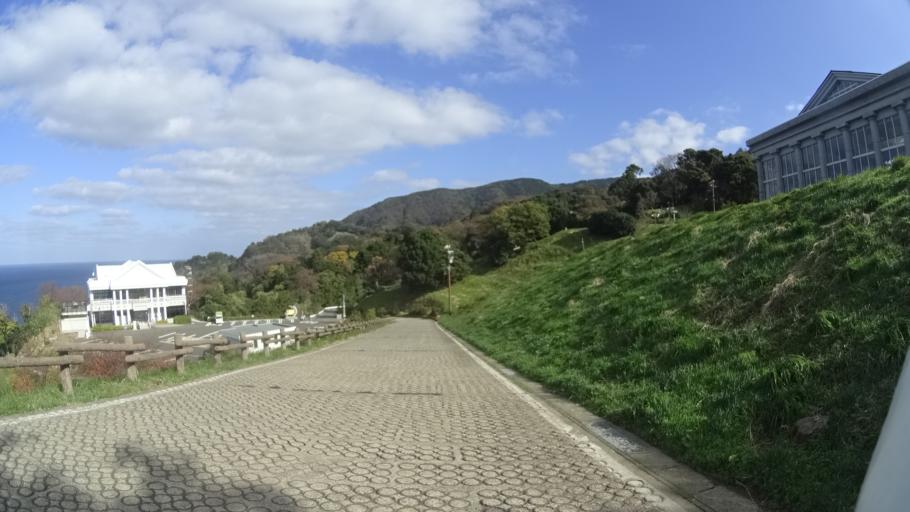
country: JP
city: Asahi
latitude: 35.9814
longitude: 135.9611
